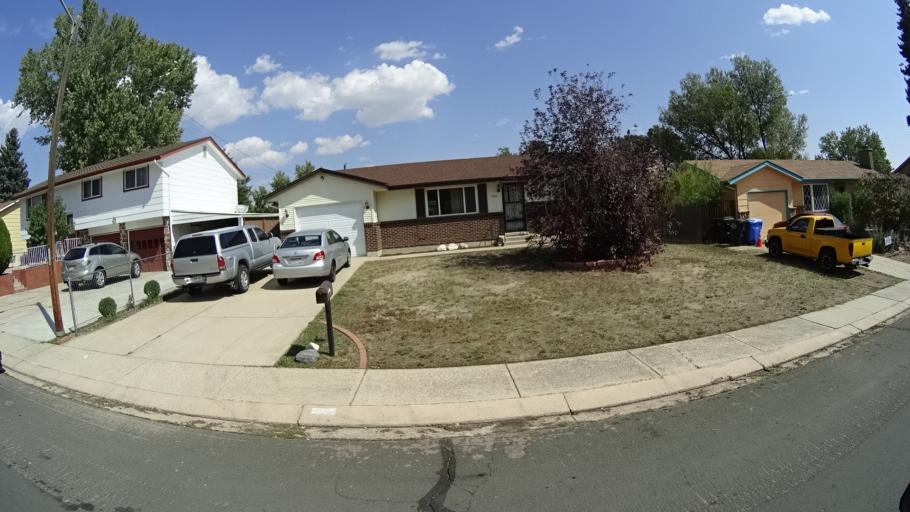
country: US
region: Colorado
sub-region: El Paso County
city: Colorado Springs
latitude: 38.8268
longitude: -104.7715
